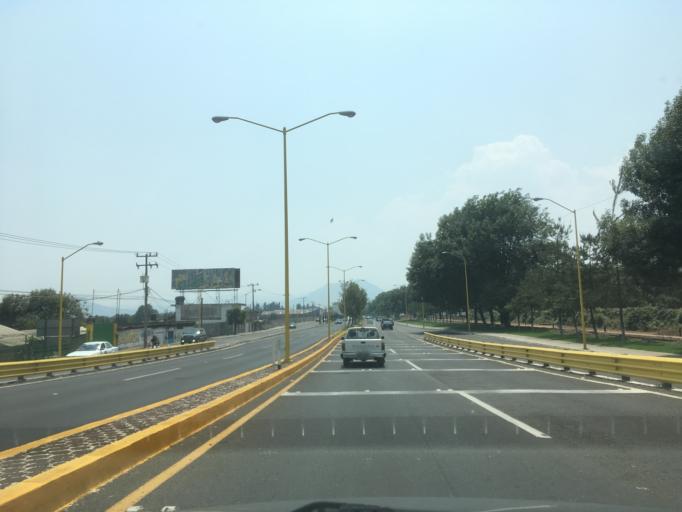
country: MX
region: Michoacan
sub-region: Uruapan
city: Toreo Bajo (El Toreo Bajo)
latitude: 19.4231
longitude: -102.0266
